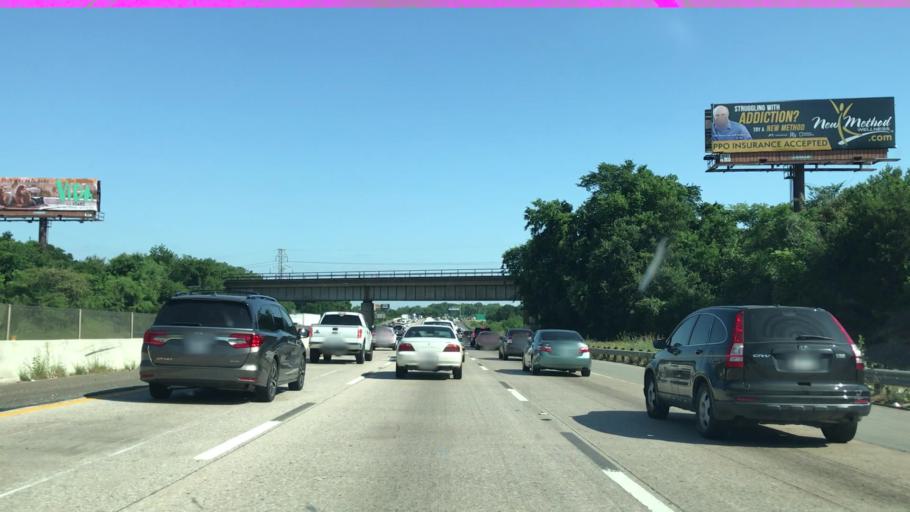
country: US
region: Texas
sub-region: Tarrant County
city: Euless
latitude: 32.8179
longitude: -97.0595
